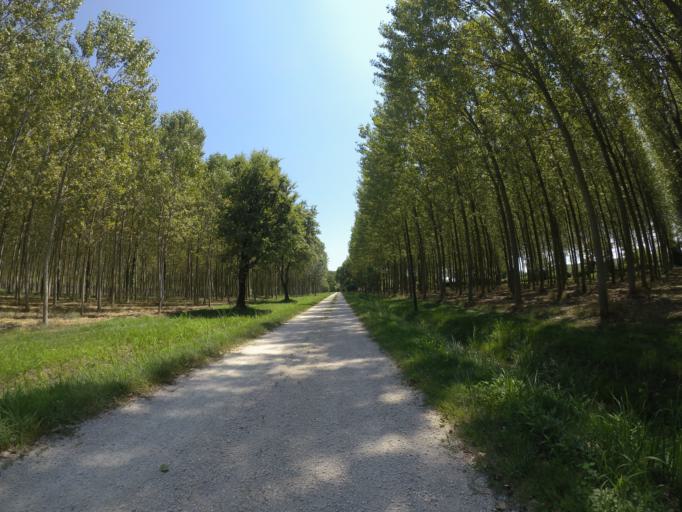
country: IT
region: Friuli Venezia Giulia
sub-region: Provincia di Udine
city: Bertiolo
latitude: 45.9304
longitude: 13.0122
